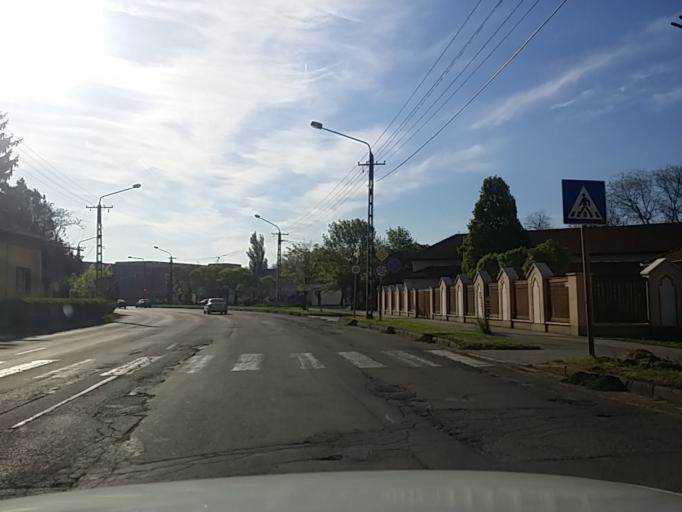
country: HU
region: Jasz-Nagykun-Szolnok
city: Torokszentmiklos
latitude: 47.1779
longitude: 20.4011
